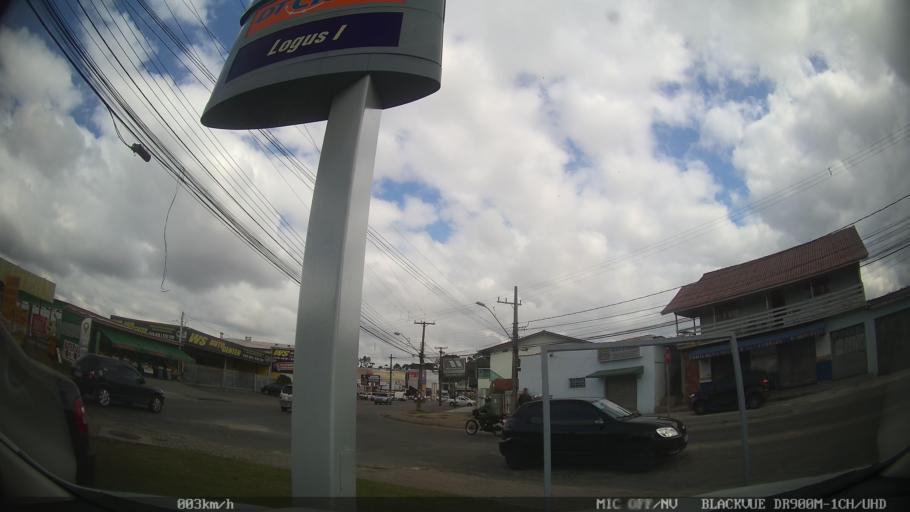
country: BR
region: Parana
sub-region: Colombo
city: Colombo
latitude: -25.3627
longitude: -49.2093
